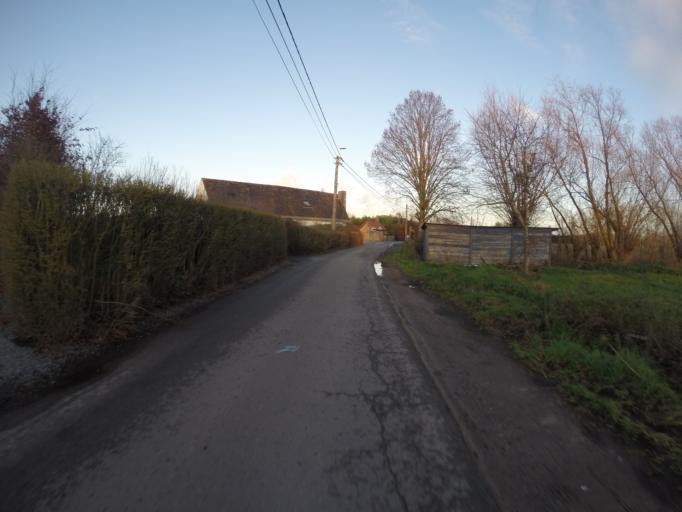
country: BE
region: Flanders
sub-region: Provincie Oost-Vlaanderen
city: Aalter
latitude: 51.0604
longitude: 3.4671
